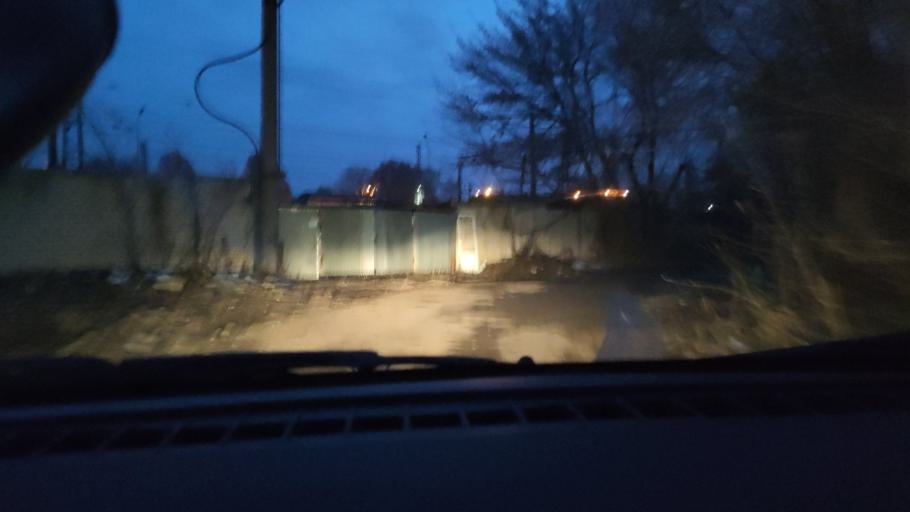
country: RU
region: Samara
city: Samara
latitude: 53.2123
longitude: 50.2660
